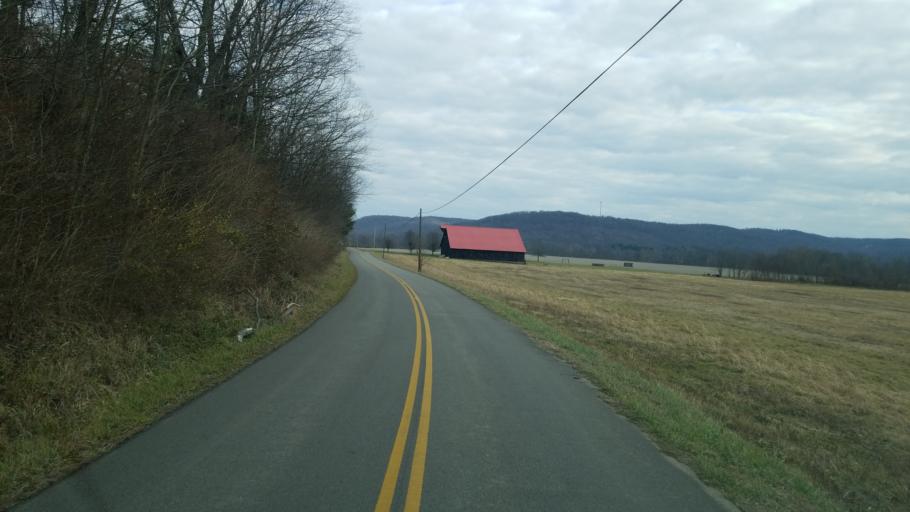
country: US
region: Ohio
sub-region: Highland County
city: Greenfield
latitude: 39.2272
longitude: -83.3060
